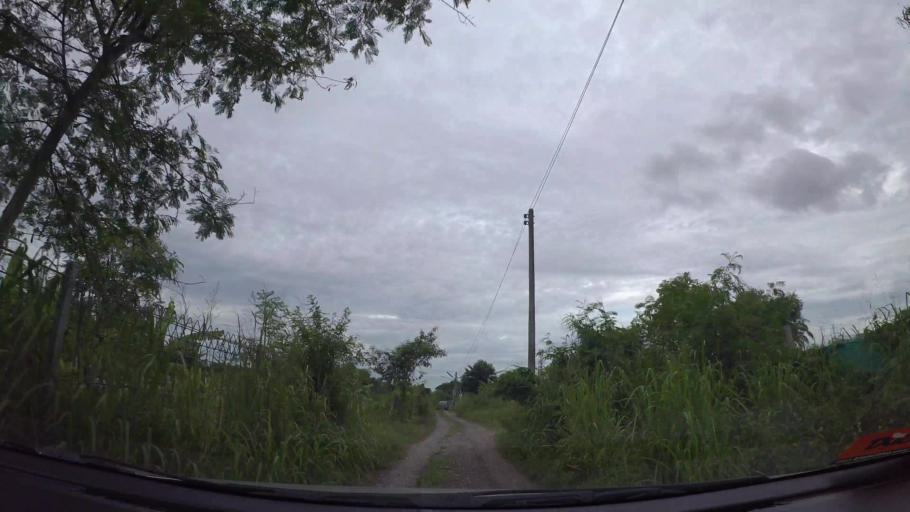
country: TH
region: Chon Buri
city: Si Racha
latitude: 13.1373
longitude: 100.9448
